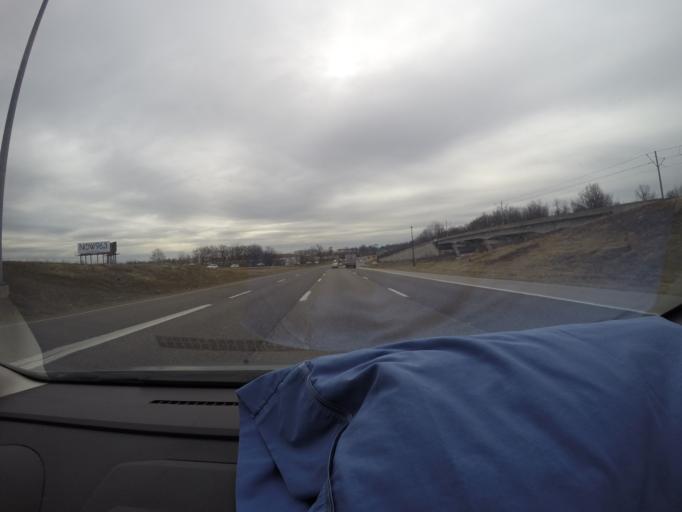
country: US
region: Missouri
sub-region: Saint Louis County
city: Bel-Ridge
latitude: 38.7276
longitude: -90.3296
